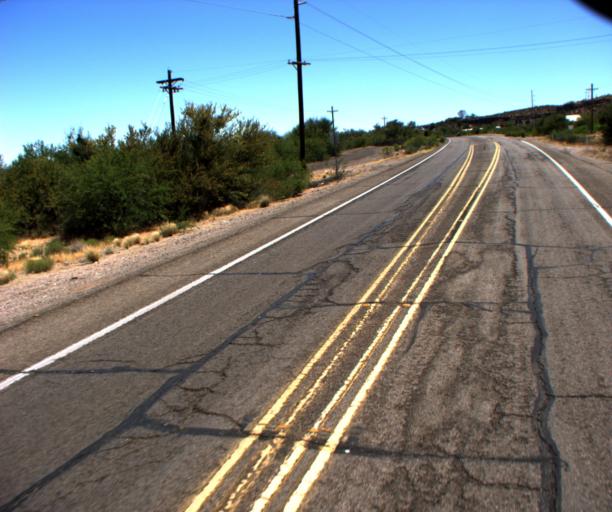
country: US
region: Arizona
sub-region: Pinal County
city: Mammoth
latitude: 32.7396
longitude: -110.6489
